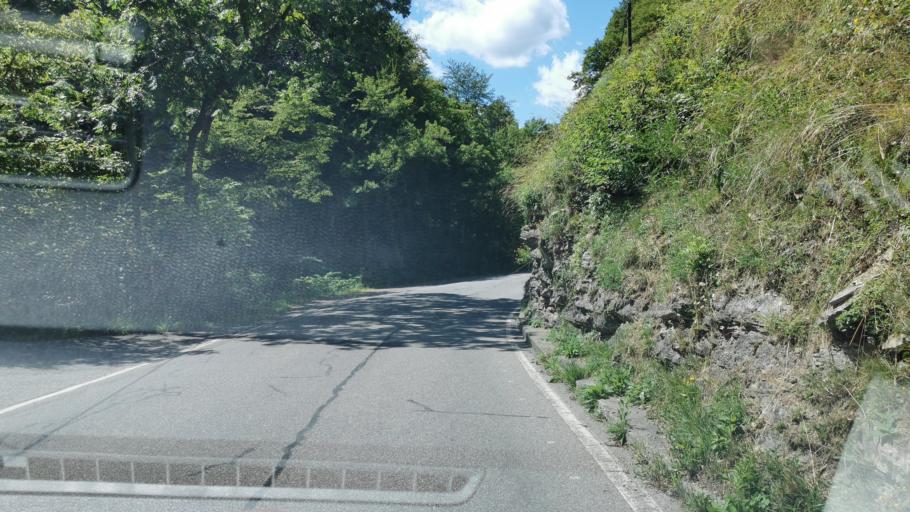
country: IT
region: Lombardy
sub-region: Provincia di Como
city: Lanzo d'Intelvi
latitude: 45.9597
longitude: 9.0024
